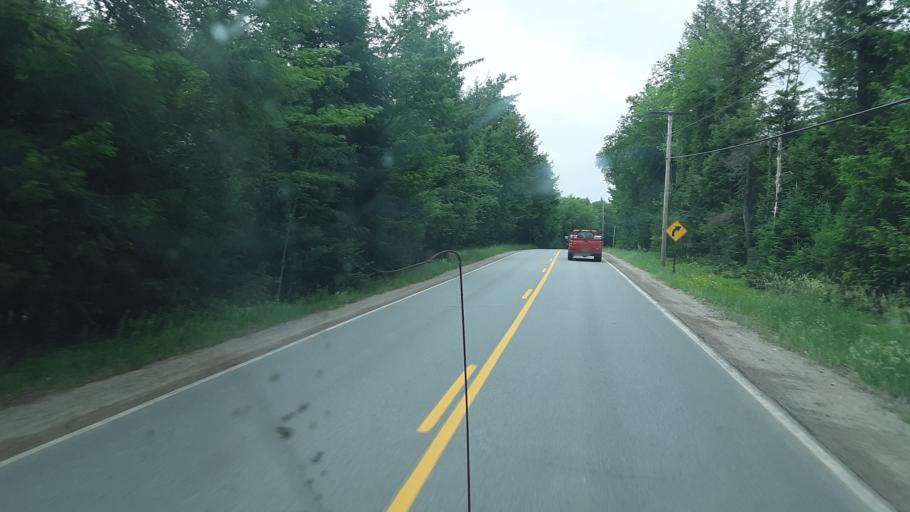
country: US
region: Maine
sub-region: Penobscot County
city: Millinocket
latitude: 45.6800
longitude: -68.7508
